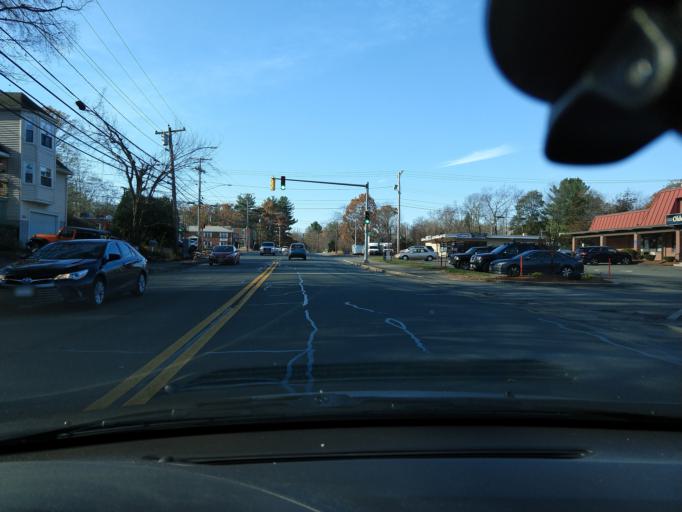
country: US
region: Massachusetts
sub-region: Middlesex County
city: Burlington
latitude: 42.5147
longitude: -71.2044
